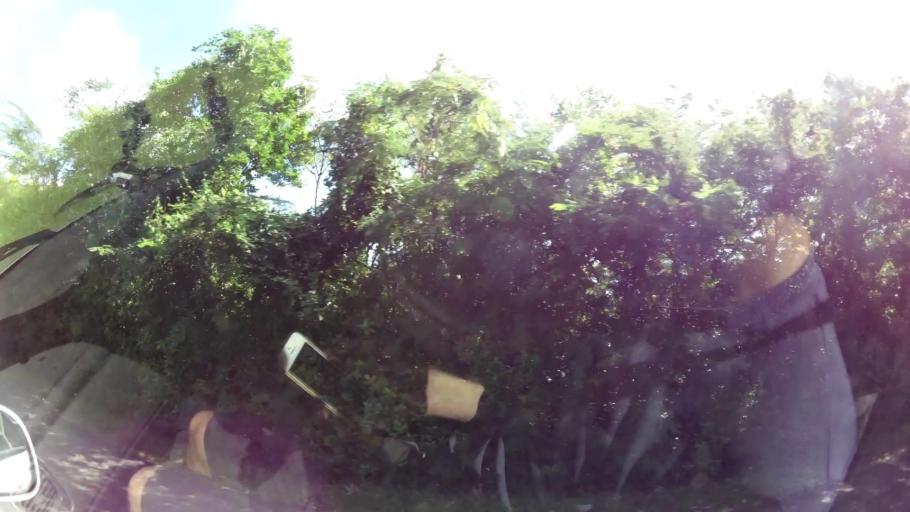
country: GD
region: Saint George
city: Saint George's
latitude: 11.9931
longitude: -61.7589
